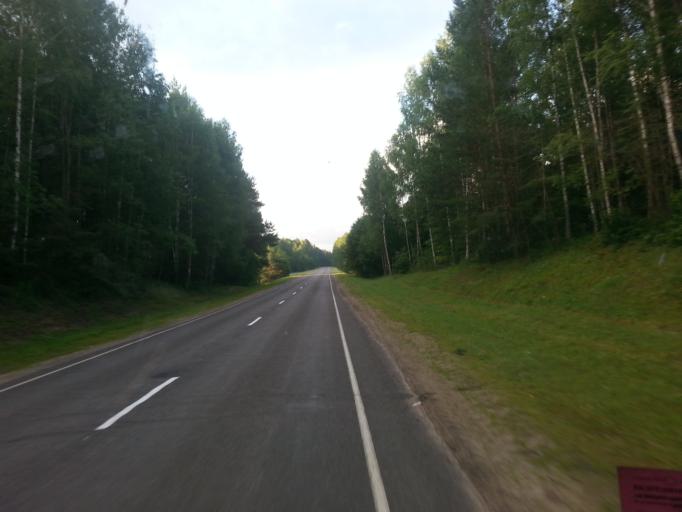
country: BY
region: Minsk
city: Kryvichy
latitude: 54.6018
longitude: 27.1852
